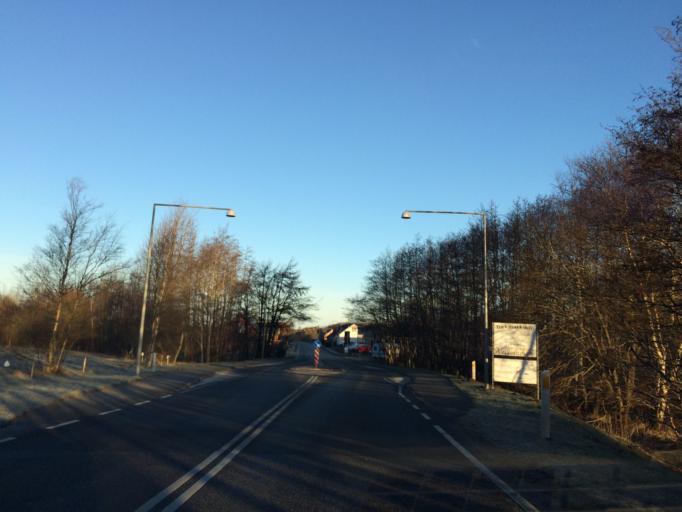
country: DK
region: Central Jutland
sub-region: Holstebro Kommune
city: Ulfborg
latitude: 56.4067
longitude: 8.3138
